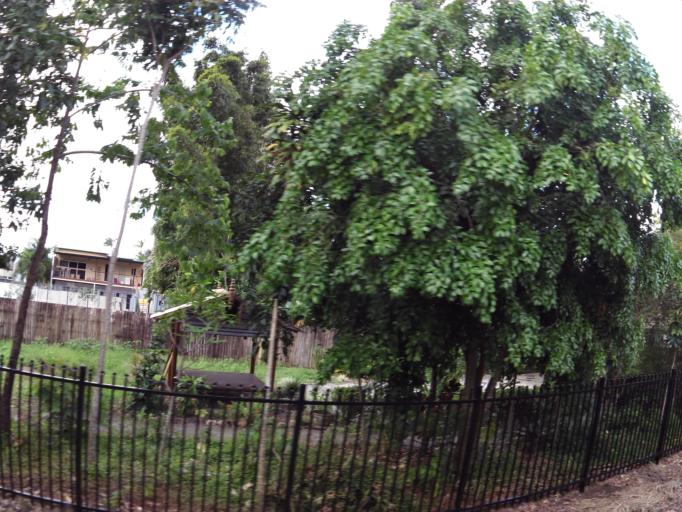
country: AU
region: Queensland
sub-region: Cairns
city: Cairns
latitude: -16.9077
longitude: 145.7569
